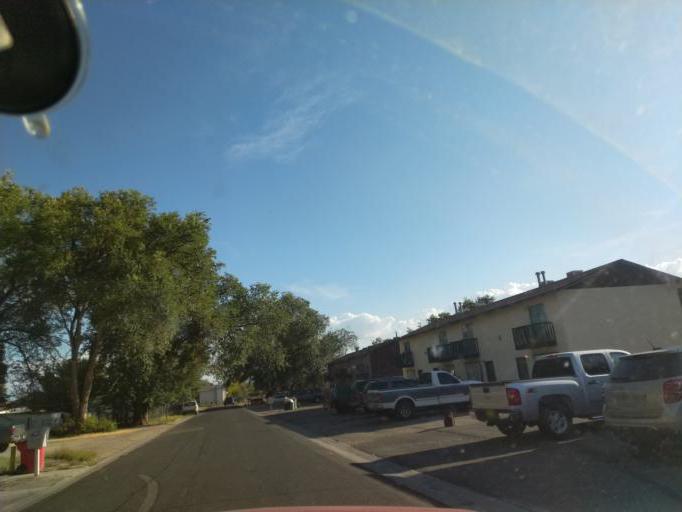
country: US
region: Colorado
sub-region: Mesa County
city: Clifton
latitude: 39.0713
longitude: -108.4571
